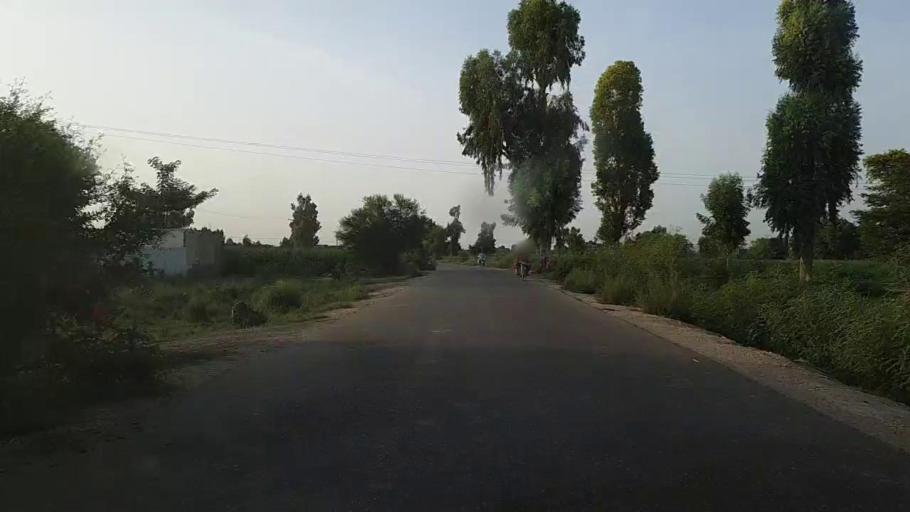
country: PK
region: Sindh
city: Ubauro
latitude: 28.1885
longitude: 69.8274
